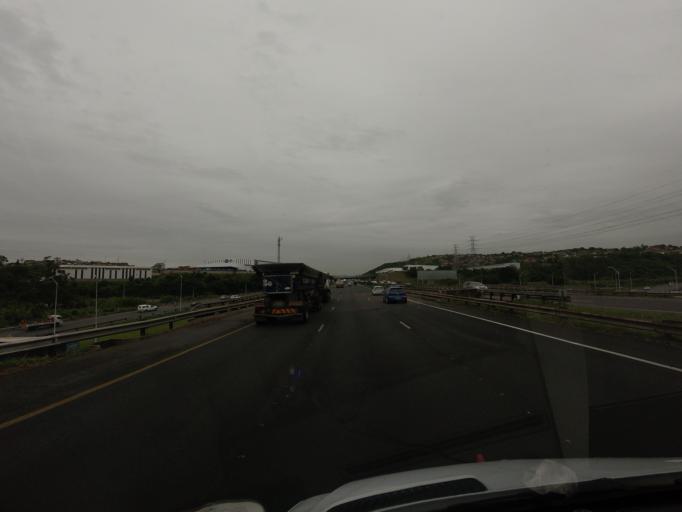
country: ZA
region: KwaZulu-Natal
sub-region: eThekwini Metropolitan Municipality
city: Berea
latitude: -29.7568
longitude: 31.0172
